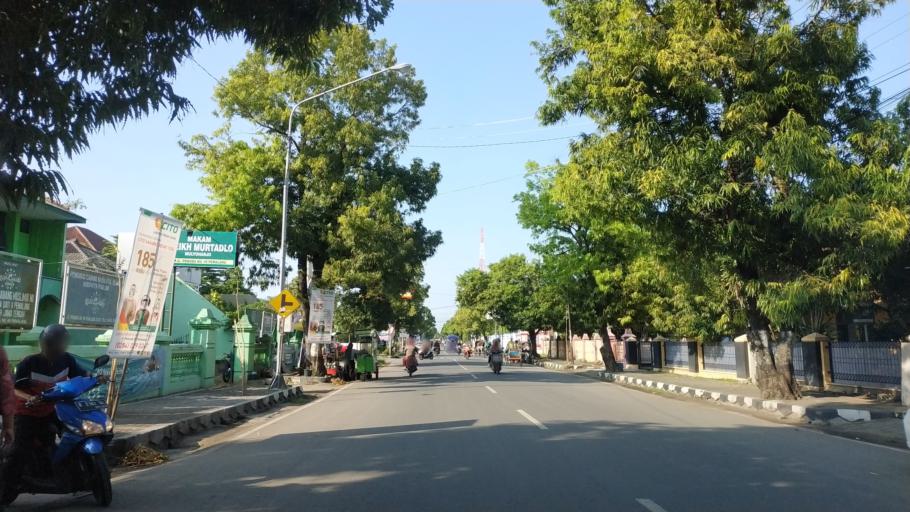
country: ID
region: Central Java
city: Pemalang
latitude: -6.8963
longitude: 109.3881
